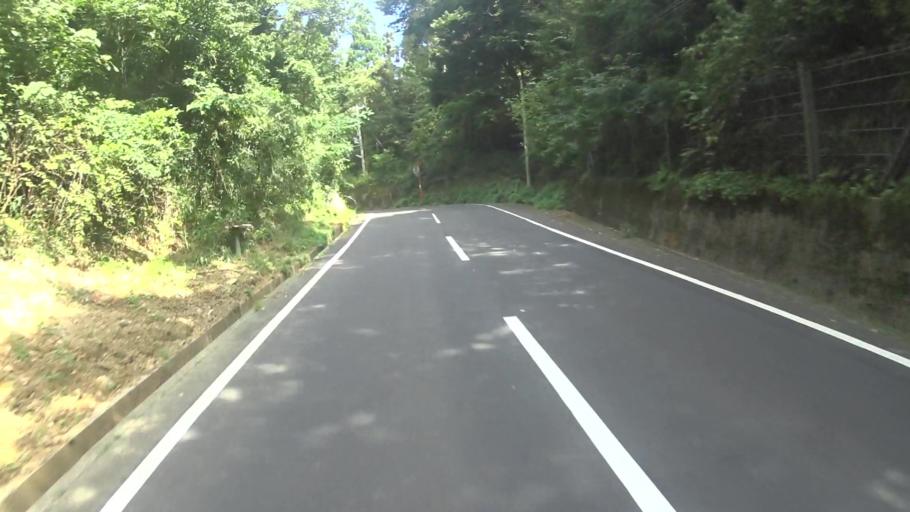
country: JP
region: Kyoto
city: Miyazu
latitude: 35.7466
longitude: 135.2451
